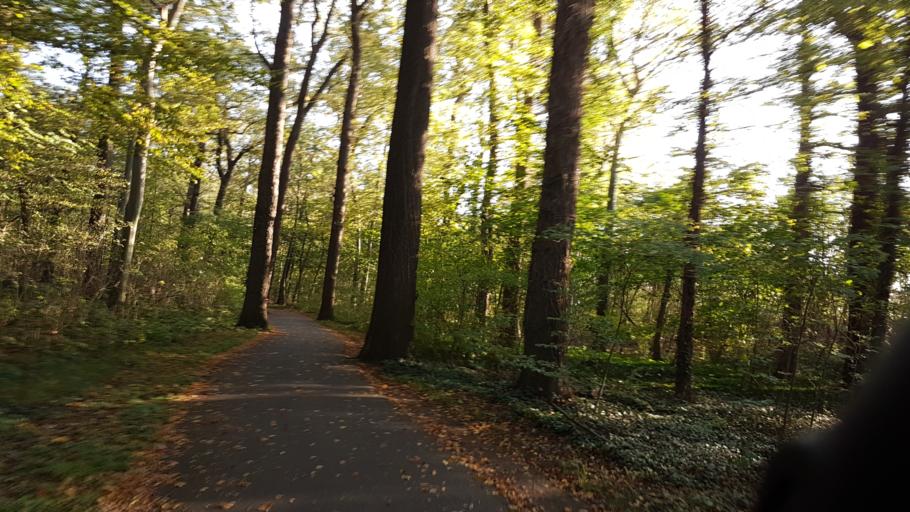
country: DE
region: Lower Saxony
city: Hannover
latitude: 52.3685
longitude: 9.7798
